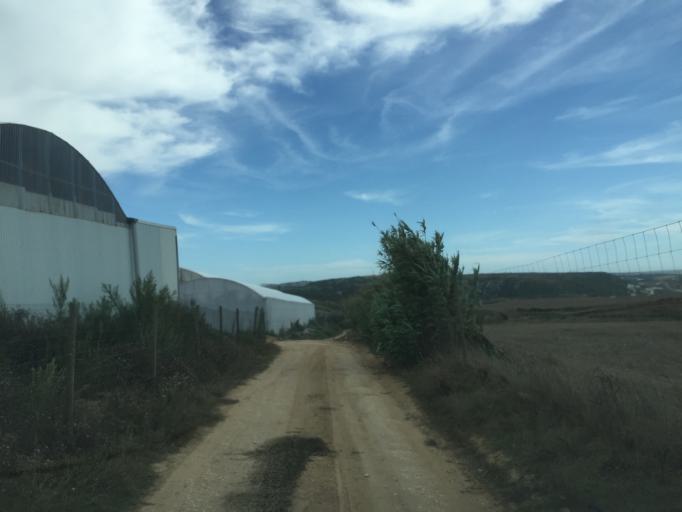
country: PT
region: Lisbon
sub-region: Lourinha
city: Lourinha
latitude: 39.1895
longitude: -9.3465
